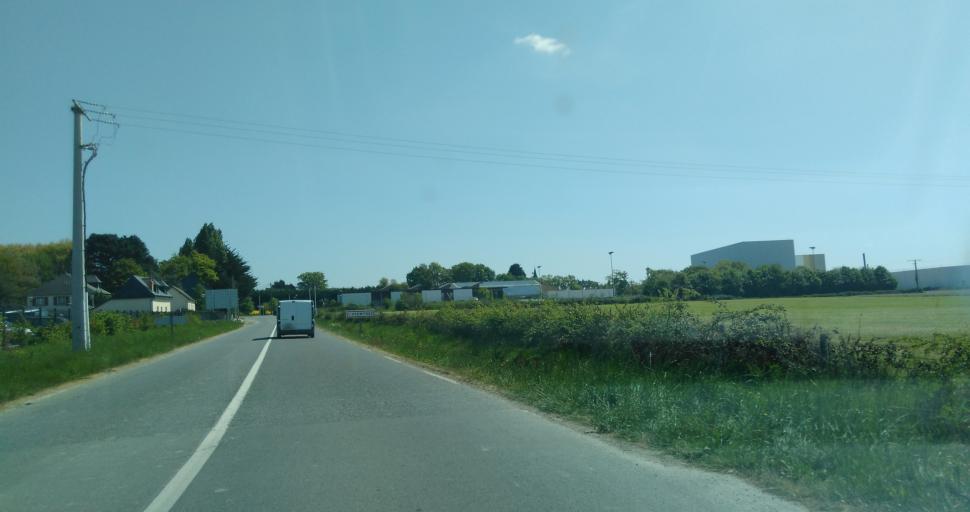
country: FR
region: Brittany
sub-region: Departement d'Ille-et-Vilaine
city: Saint-Gilles
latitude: 48.1284
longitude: -1.8278
